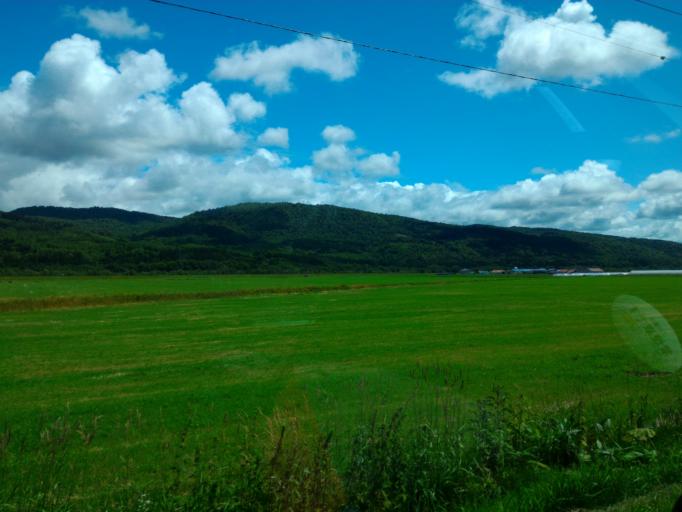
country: JP
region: Hokkaido
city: Nayoro
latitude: 44.5705
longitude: 142.3141
